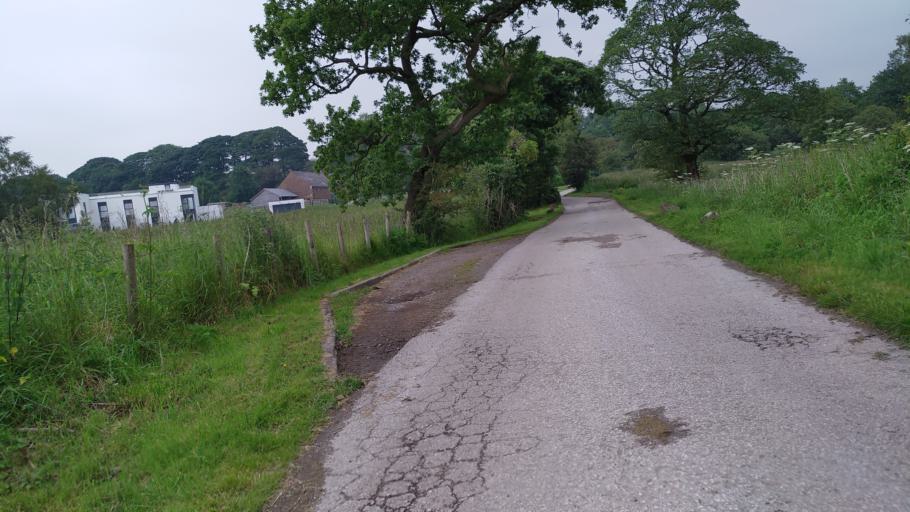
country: GB
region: England
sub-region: Lancashire
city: Chorley
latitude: 53.6756
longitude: -2.5875
